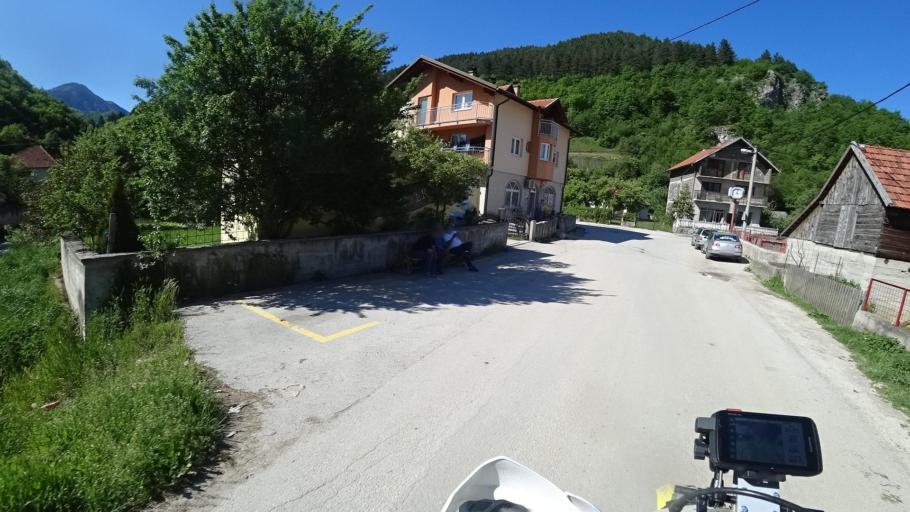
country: BA
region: Federation of Bosnia and Herzegovina
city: Travnik
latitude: 44.2716
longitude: 17.7329
